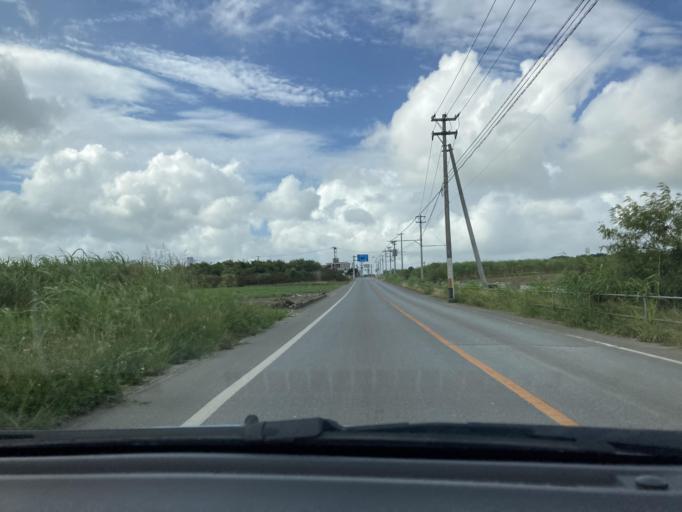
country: JP
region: Okinawa
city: Itoman
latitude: 26.1005
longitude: 127.6977
